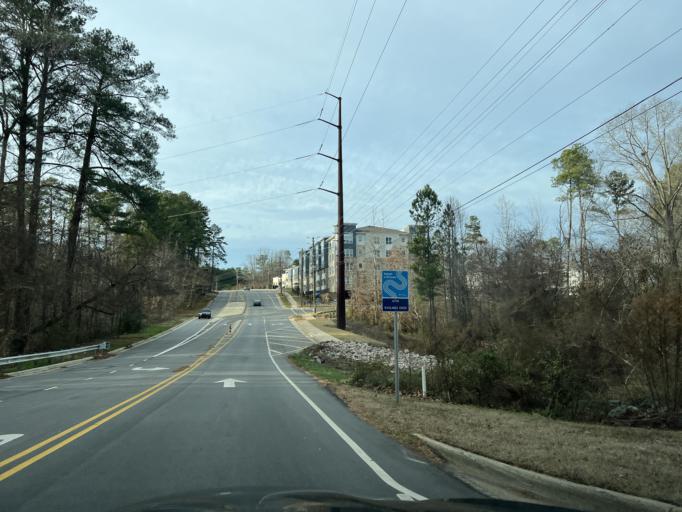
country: US
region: North Carolina
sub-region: Wake County
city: Cary
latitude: 35.8039
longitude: -78.7351
